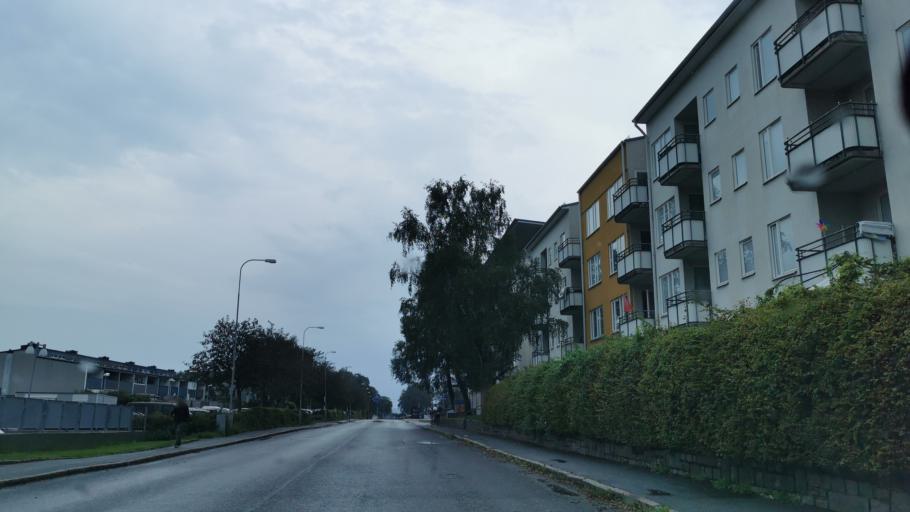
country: SE
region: Vaestra Goetaland
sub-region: Goteborg
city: Majorna
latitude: 57.6723
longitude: 11.9119
